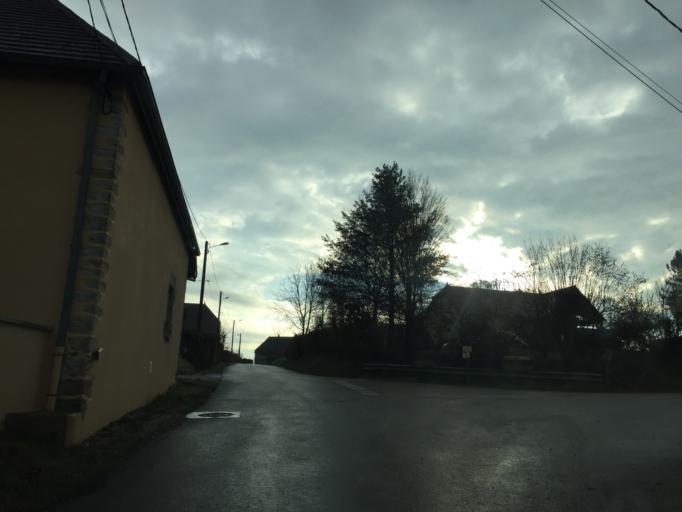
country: FR
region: Franche-Comte
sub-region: Departement du Jura
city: Mont-sous-Vaudrey
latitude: 46.9794
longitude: 5.5841
